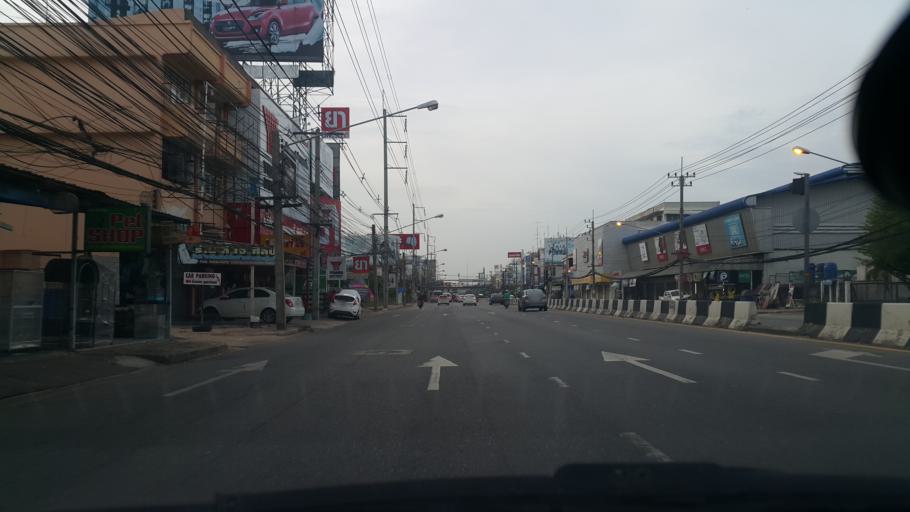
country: TH
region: Chon Buri
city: Phatthaya
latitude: 12.9648
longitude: 100.9097
